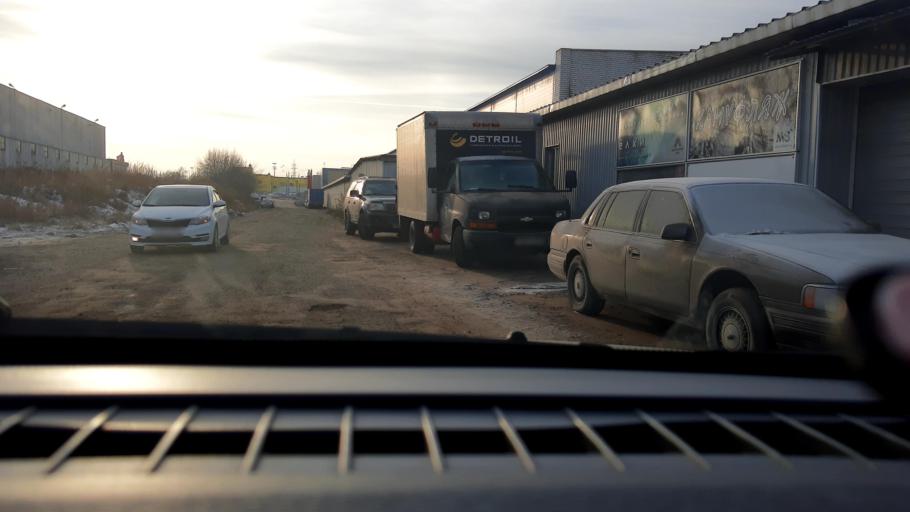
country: RU
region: Nizjnij Novgorod
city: Nizhniy Novgorod
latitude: 56.3052
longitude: 43.9481
